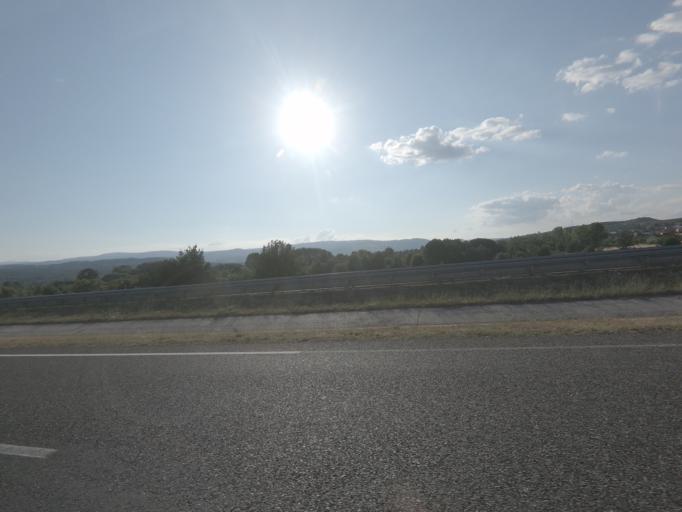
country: ES
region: Galicia
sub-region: Provincia de Ourense
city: Oimbra
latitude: 41.8437
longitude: -7.4136
